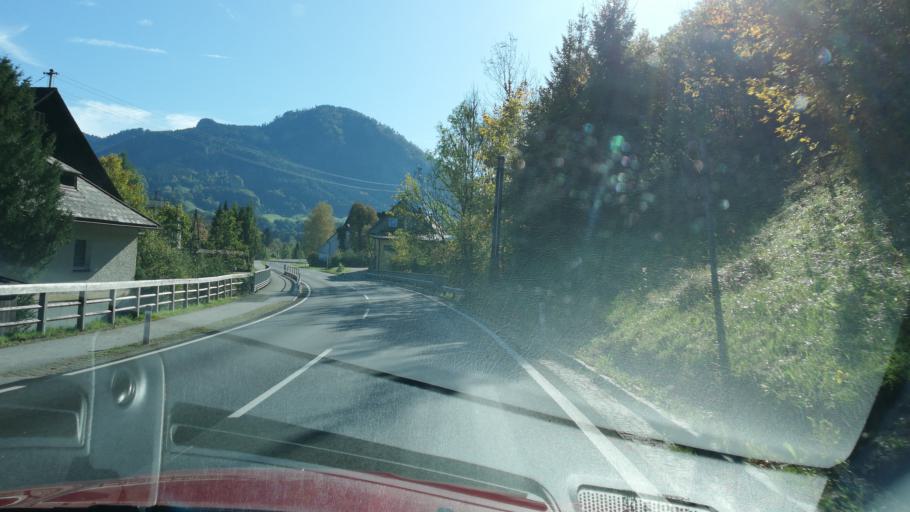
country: AT
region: Styria
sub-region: Politischer Bezirk Liezen
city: Landl
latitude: 47.6496
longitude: 14.7479
